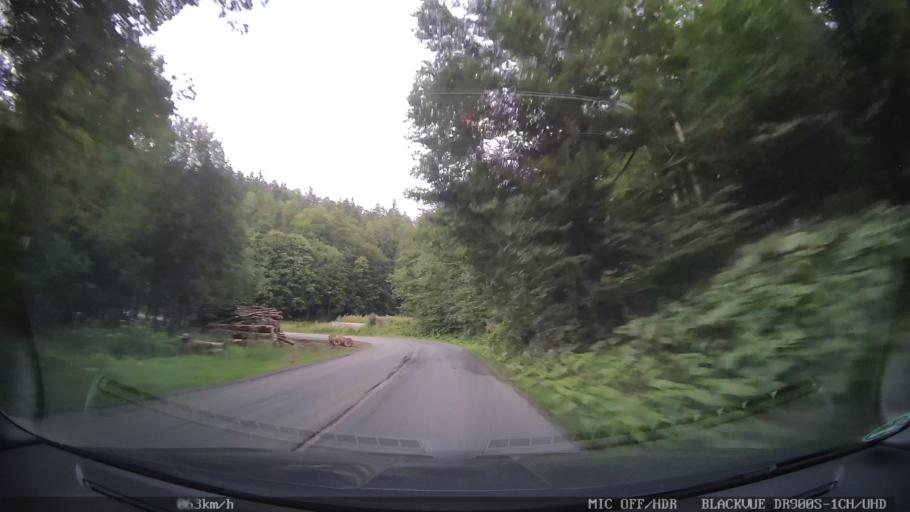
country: HR
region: Primorsko-Goranska
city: Vrbovsko
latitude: 45.2032
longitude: 15.0148
